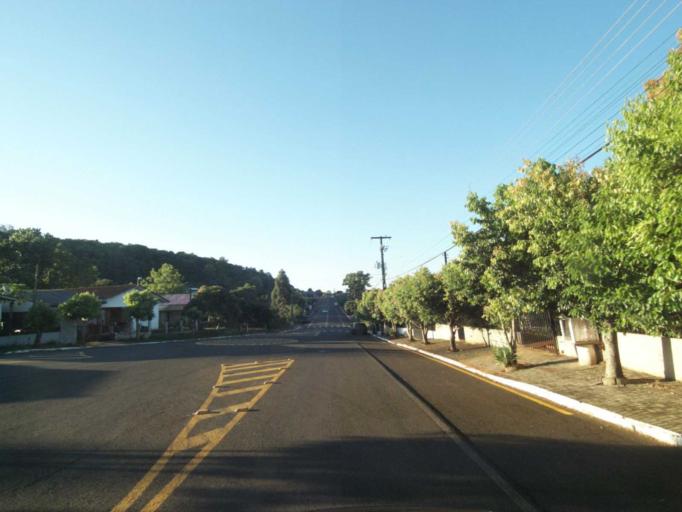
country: BR
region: Parana
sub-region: Coronel Vivida
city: Coronel Vivida
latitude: -25.9586
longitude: -52.8167
